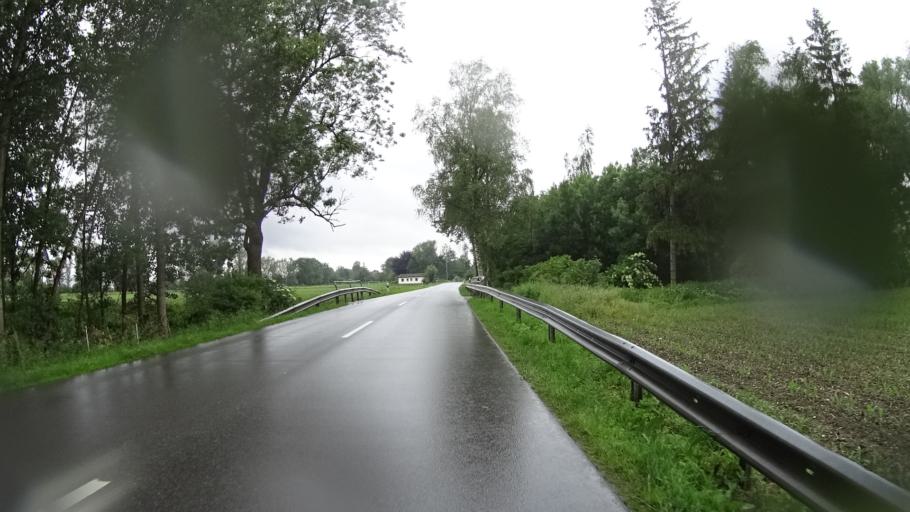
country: AT
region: Upper Austria
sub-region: Politischer Bezirk Scharding
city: Scharding
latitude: 48.4454
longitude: 13.4069
